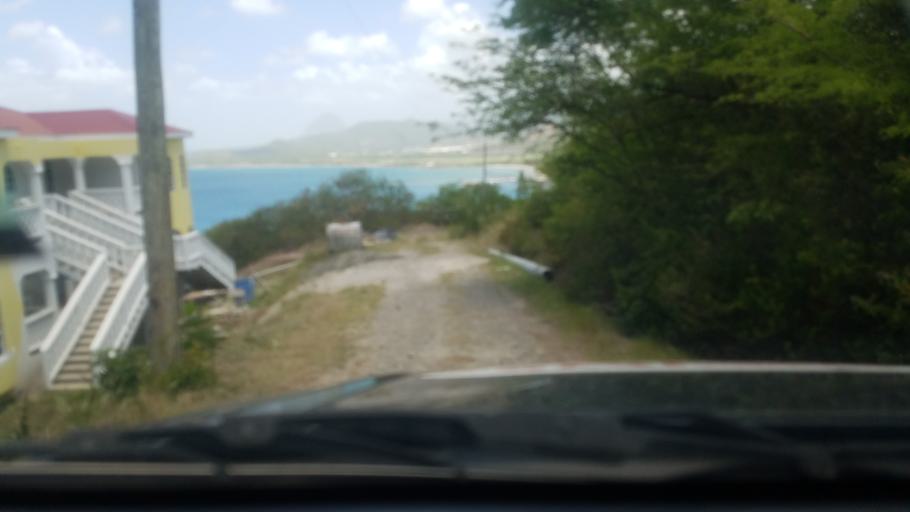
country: LC
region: Vieux-Fort
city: Vieux Fort
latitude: 13.7164
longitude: -60.9501
